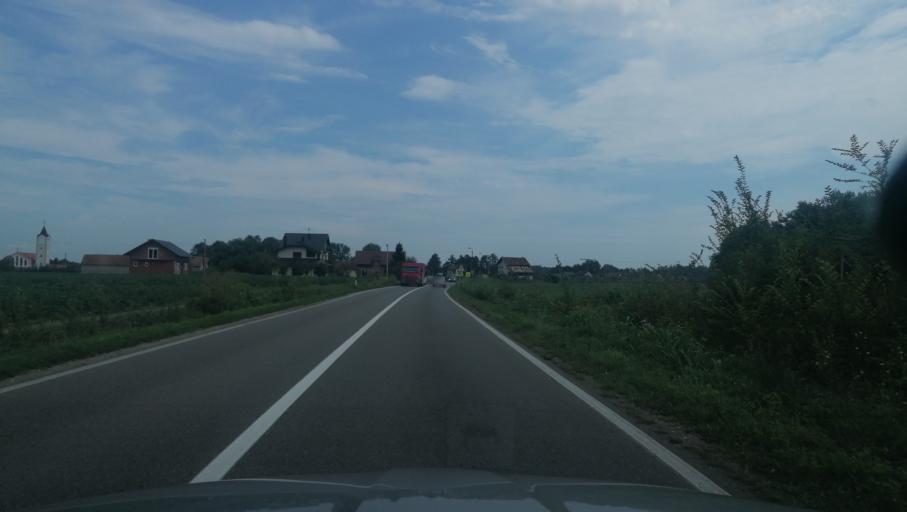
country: BA
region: Brcko
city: Brka
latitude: 44.9288
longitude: 18.7118
